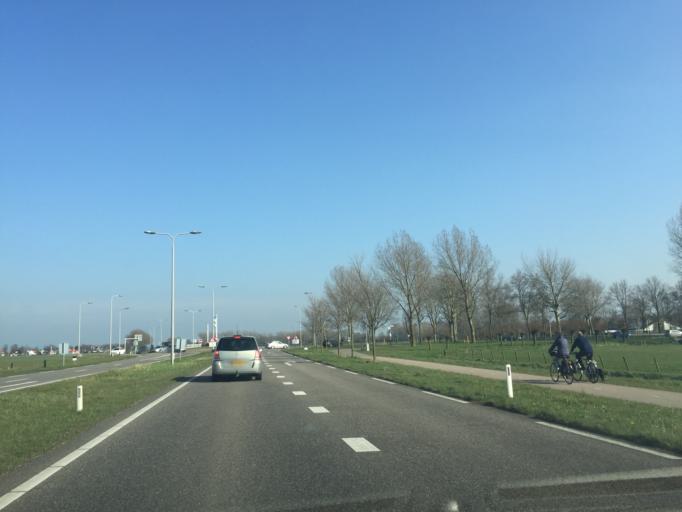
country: NL
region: North Holland
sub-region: Gemeente Castricum
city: Castricum
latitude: 52.5620
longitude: 4.6784
